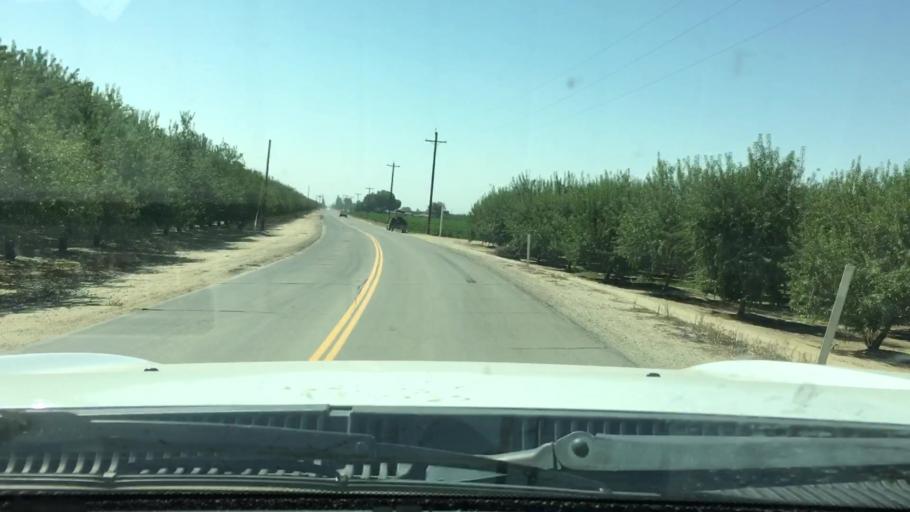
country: US
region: California
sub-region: Kern County
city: Shafter
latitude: 35.5481
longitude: -119.2776
